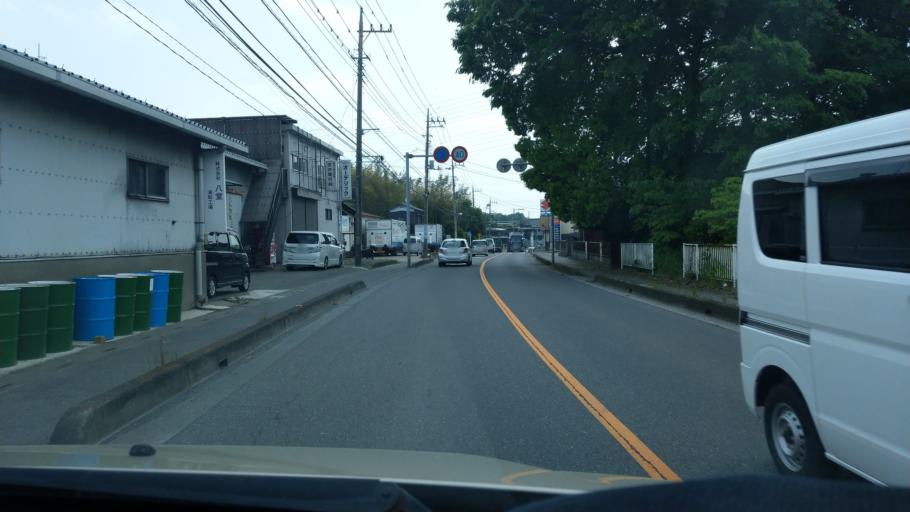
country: JP
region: Saitama
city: Saitama
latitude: 35.9090
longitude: 139.6991
